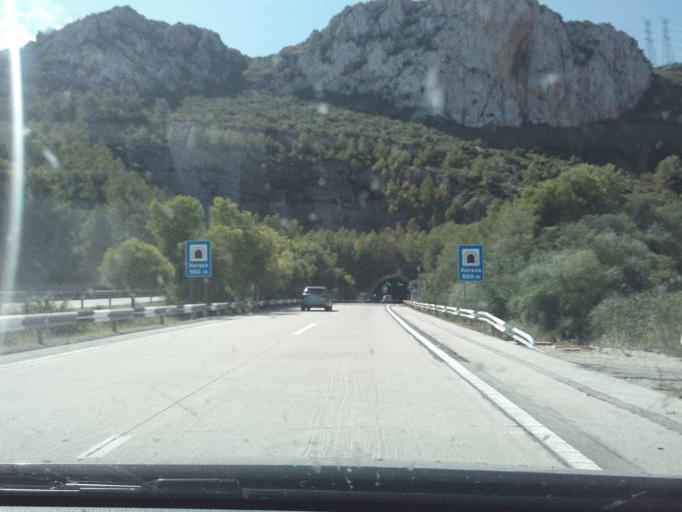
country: ES
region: Valencia
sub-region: Provincia de Valencia
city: Xeresa
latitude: 39.0047
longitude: -0.2249
